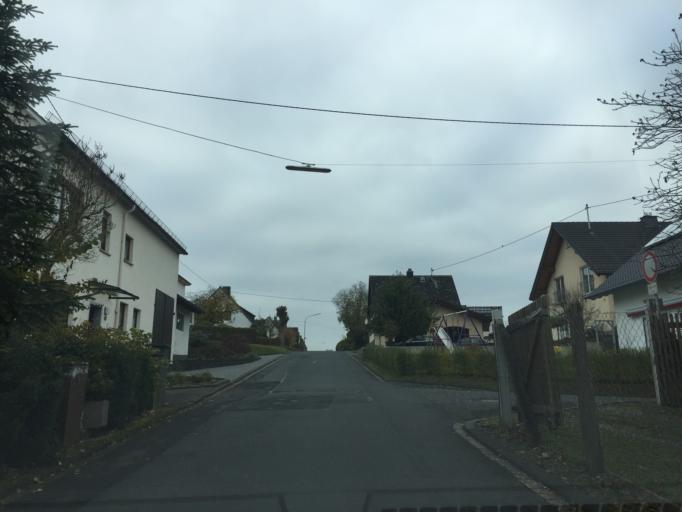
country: DE
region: Rheinland-Pfalz
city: Heiligenroth
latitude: 50.4474
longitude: 7.8642
